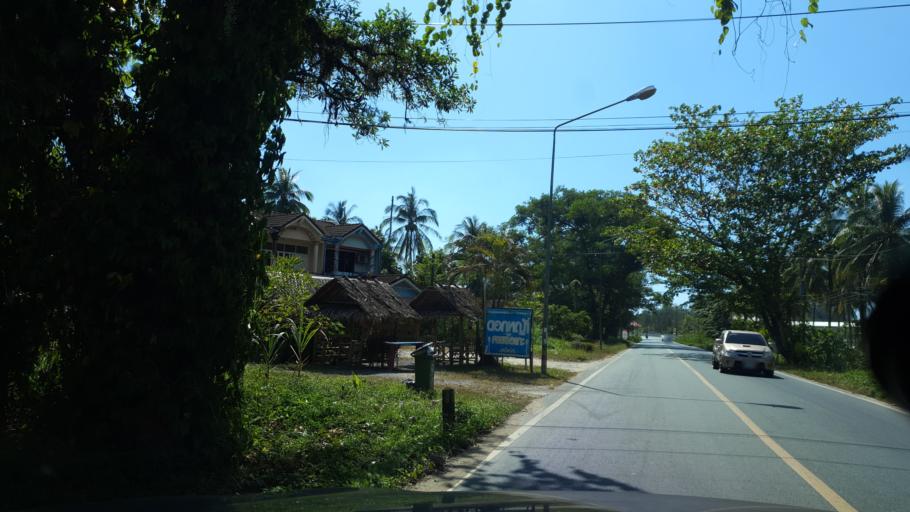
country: TH
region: Phangnga
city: Ban Khao Lak
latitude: 8.5895
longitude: 98.2517
